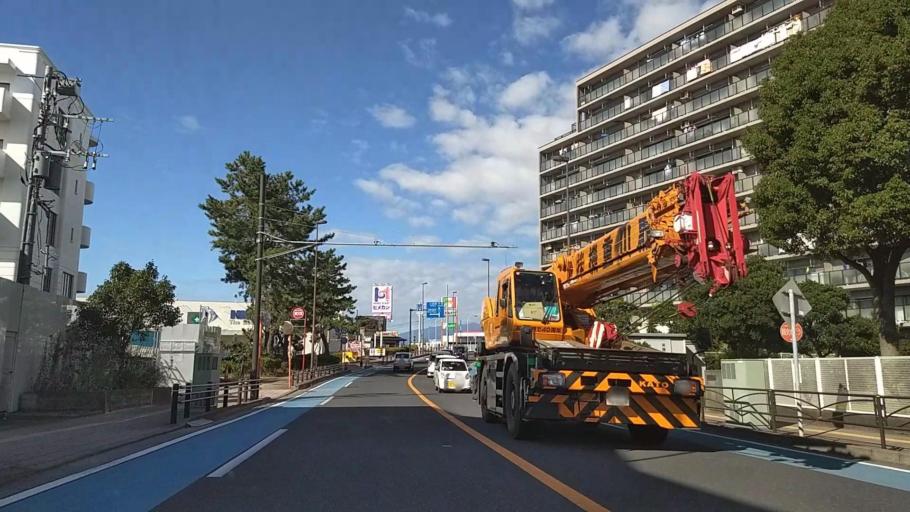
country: JP
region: Kanagawa
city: Chigasaki
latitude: 35.3288
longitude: 139.3913
